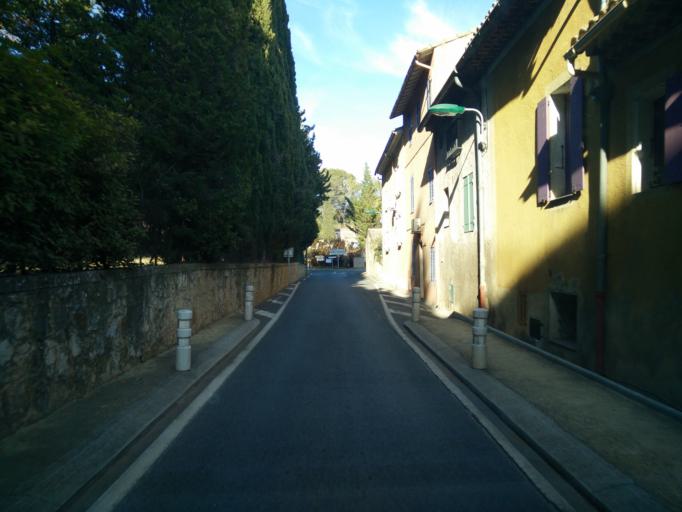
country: FR
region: Provence-Alpes-Cote d'Azur
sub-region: Departement du Var
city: Taradeau
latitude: 43.4527
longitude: 6.4238
